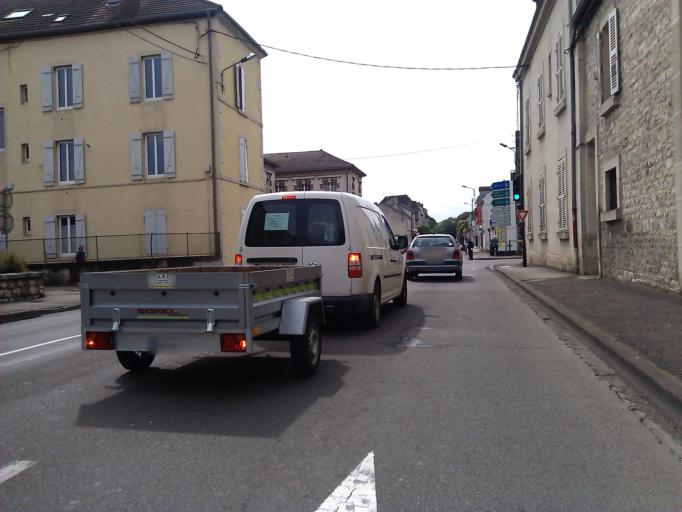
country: FR
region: Franche-Comte
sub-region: Departement du Jura
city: Dole
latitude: 47.0974
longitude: 5.4942
